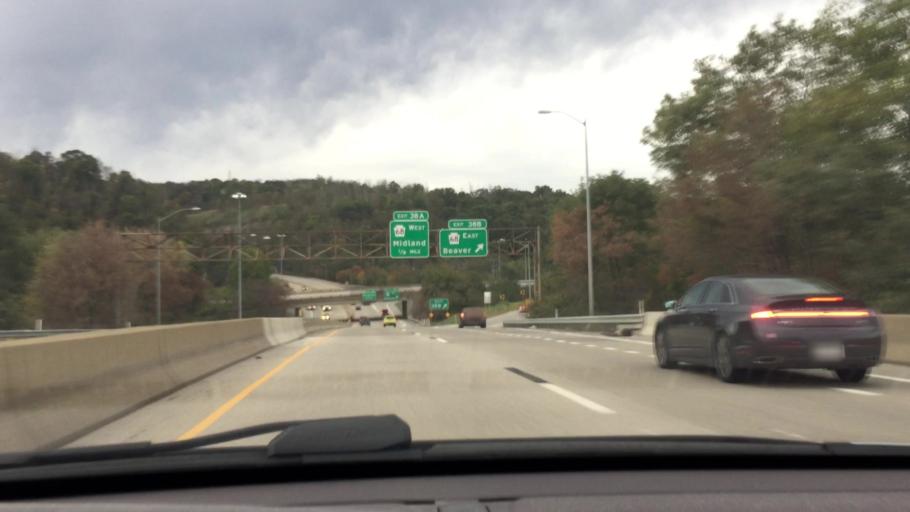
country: US
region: Pennsylvania
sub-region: Beaver County
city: Beaver
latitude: 40.6811
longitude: -80.3326
